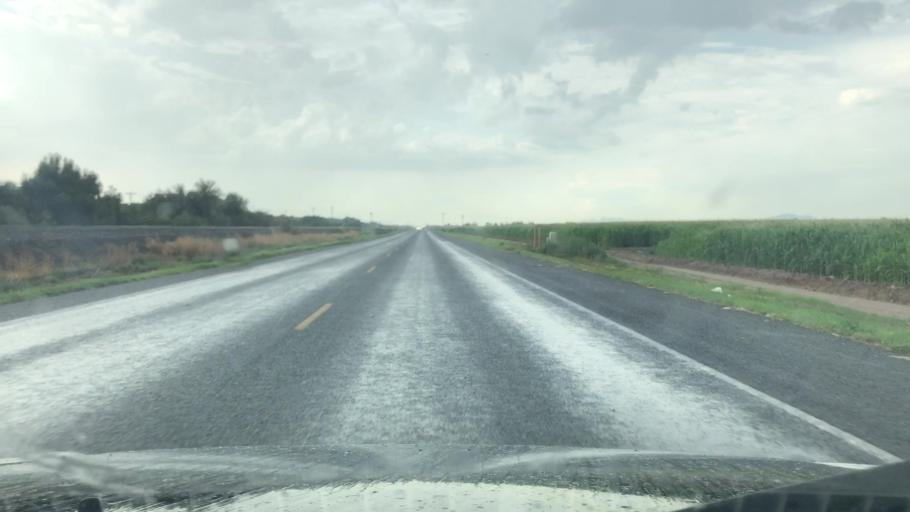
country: US
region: New Mexico
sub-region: Dona Ana County
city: Mesquite
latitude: 32.1413
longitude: -106.6819
